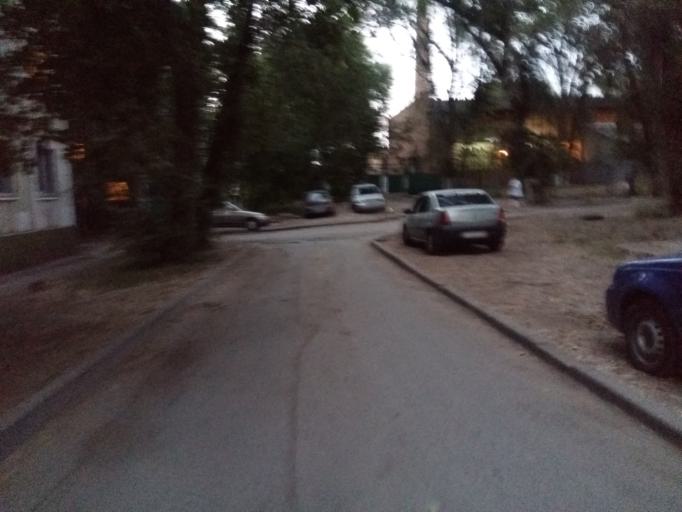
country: RU
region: Rostov
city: Imeni Chkalova
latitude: 47.2771
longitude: 39.7386
